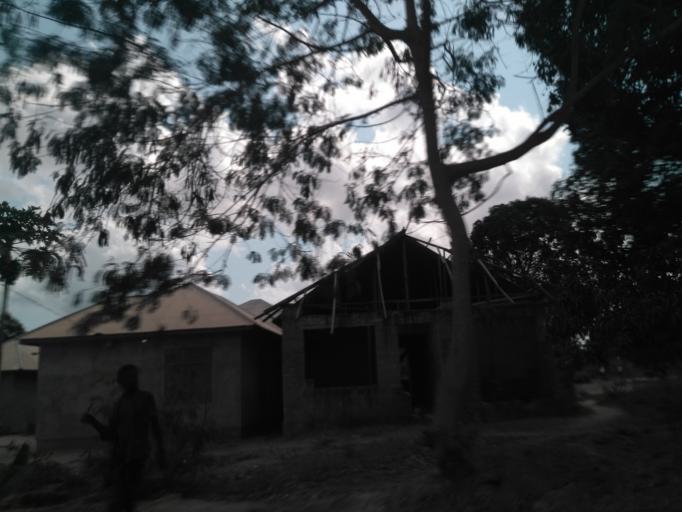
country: TZ
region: Dar es Salaam
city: Dar es Salaam
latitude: -6.8784
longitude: 39.3365
